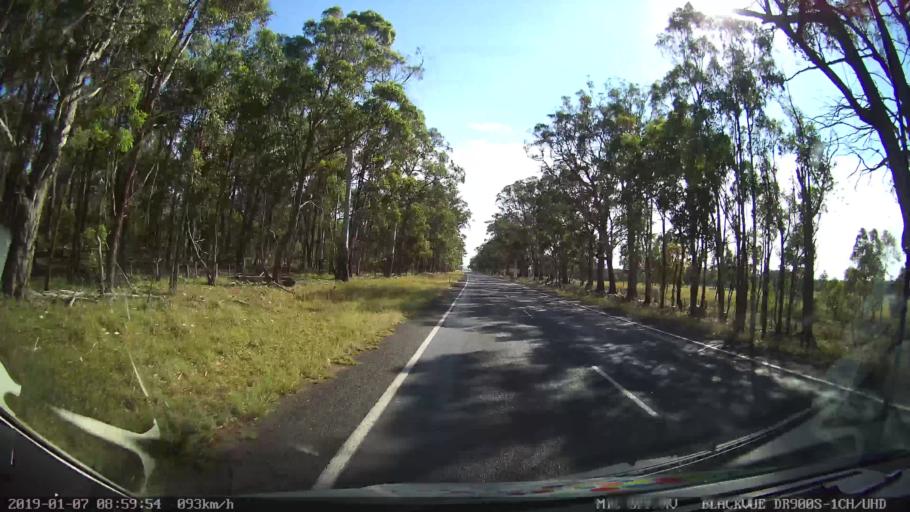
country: AU
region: New South Wales
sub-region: Armidale Dumaresq
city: Armidale
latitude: -30.7521
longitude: 151.3860
